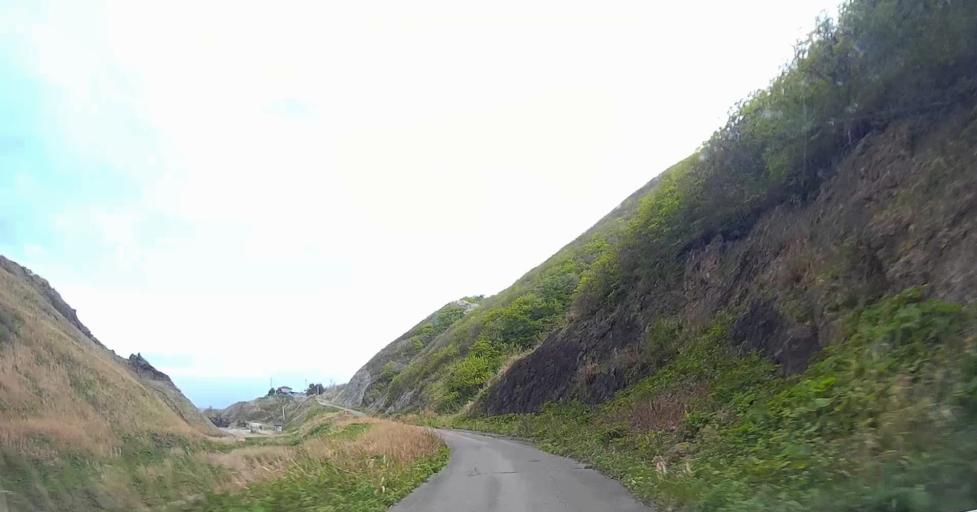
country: JP
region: Aomori
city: Shimokizukuri
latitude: 41.2404
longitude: 140.3434
